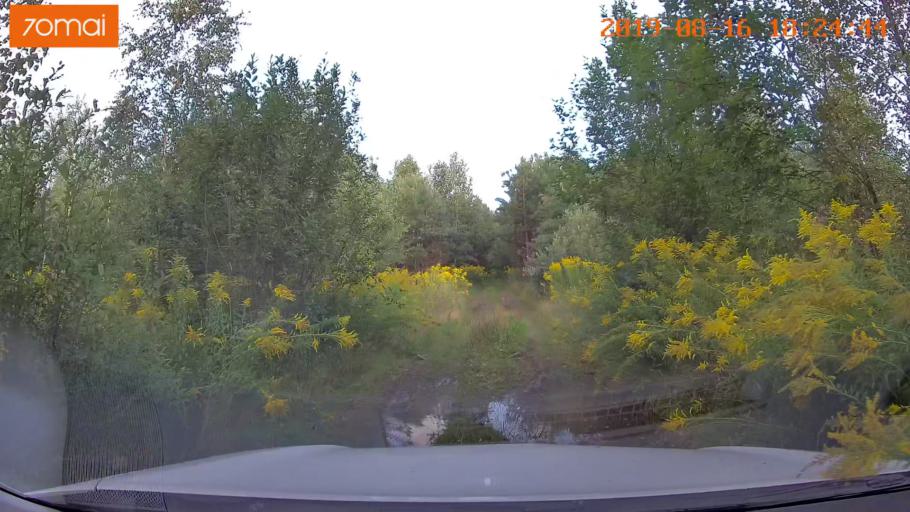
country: BY
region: Mogilev
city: Asipovichy
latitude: 53.2044
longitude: 28.6372
